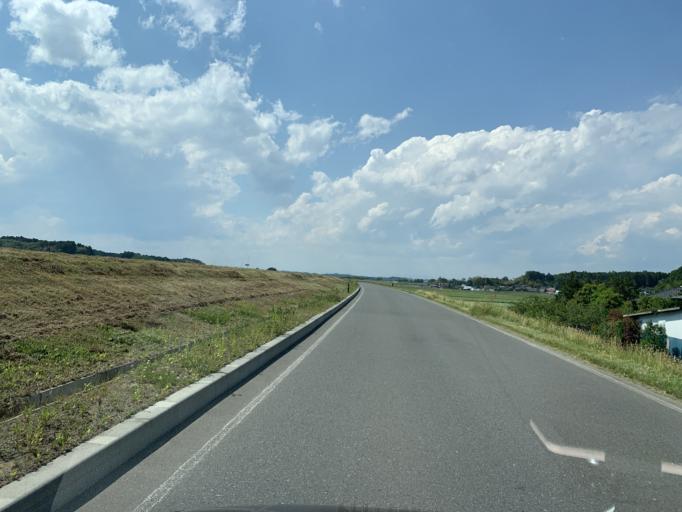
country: JP
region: Miyagi
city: Matsushima
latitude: 38.4310
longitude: 141.1236
